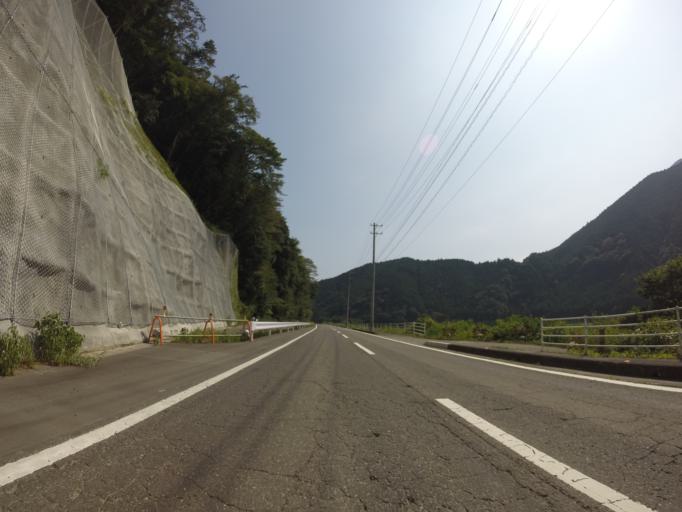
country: JP
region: Shizuoka
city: Shizuoka-shi
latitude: 35.1386
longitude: 138.3647
